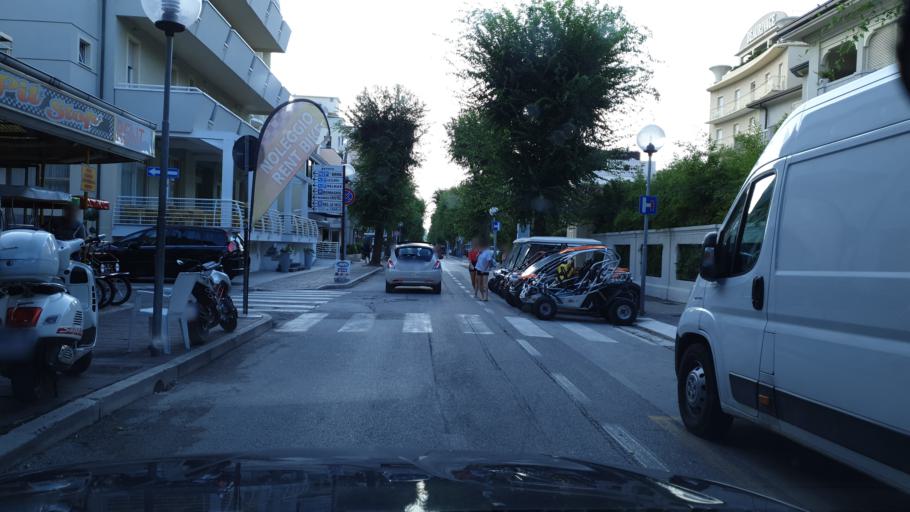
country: IT
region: Emilia-Romagna
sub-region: Provincia di Rimini
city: Cattolica
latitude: 43.9681
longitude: 12.7307
